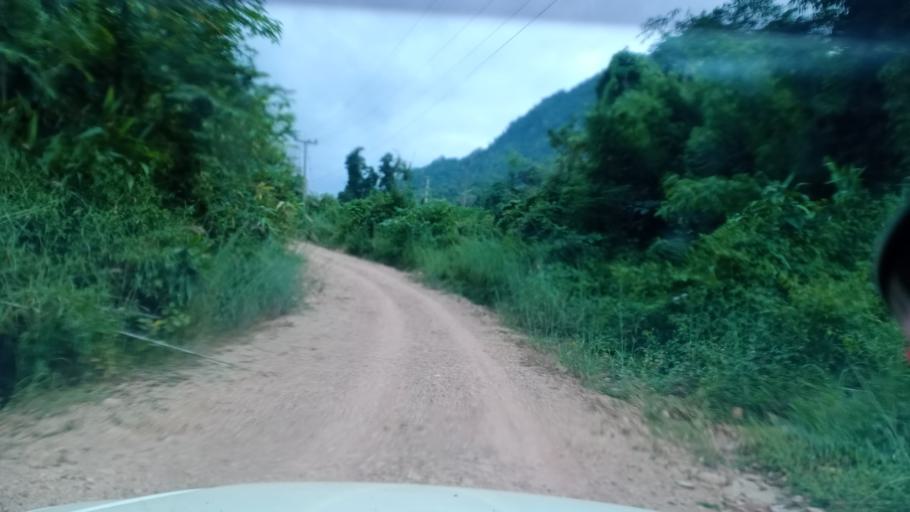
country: TH
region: Changwat Bueng Kan
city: Pak Khat
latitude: 18.7258
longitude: 103.2618
